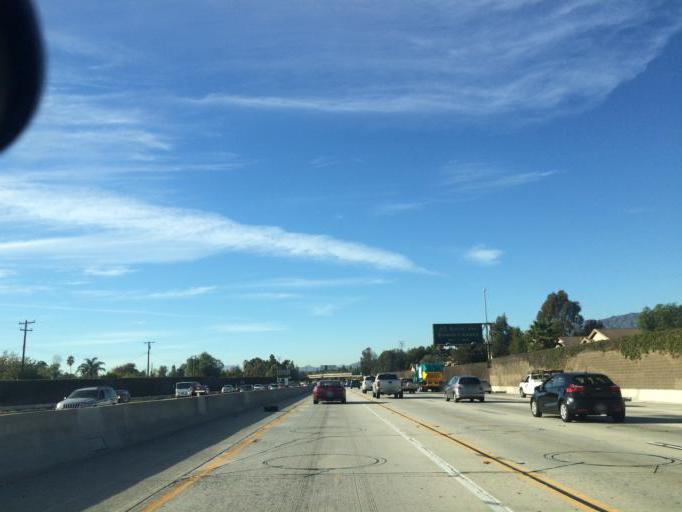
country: US
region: California
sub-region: San Bernardino County
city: Upland
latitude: 34.0826
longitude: -117.6319
